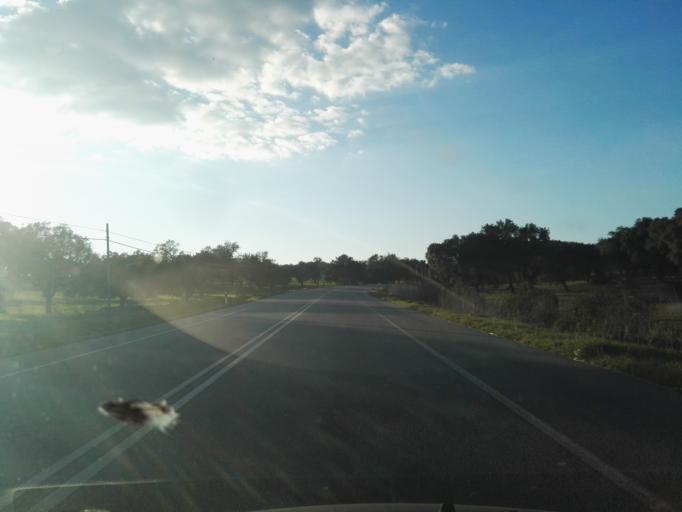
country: PT
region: Evora
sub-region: Arraiolos
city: Arraiolos
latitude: 38.6138
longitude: -8.0756
